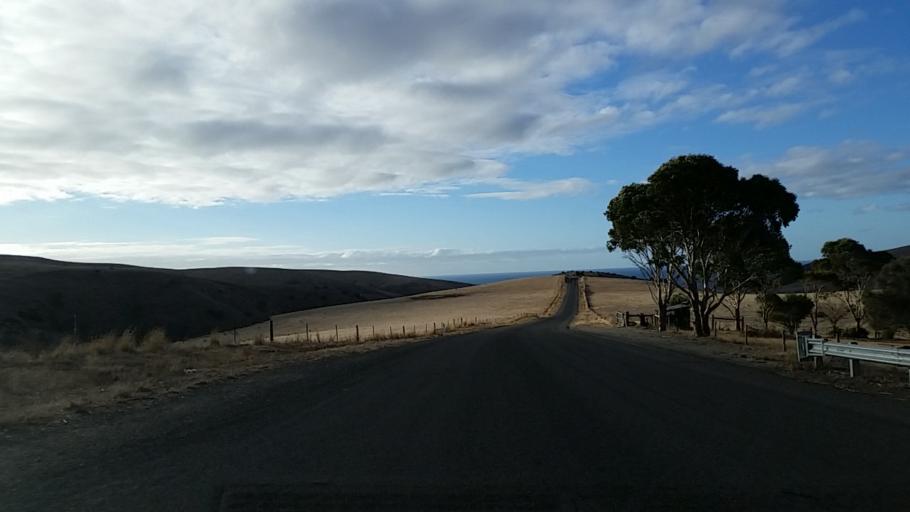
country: AU
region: South Australia
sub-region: Yankalilla
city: Normanville
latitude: -35.5521
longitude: 138.1954
